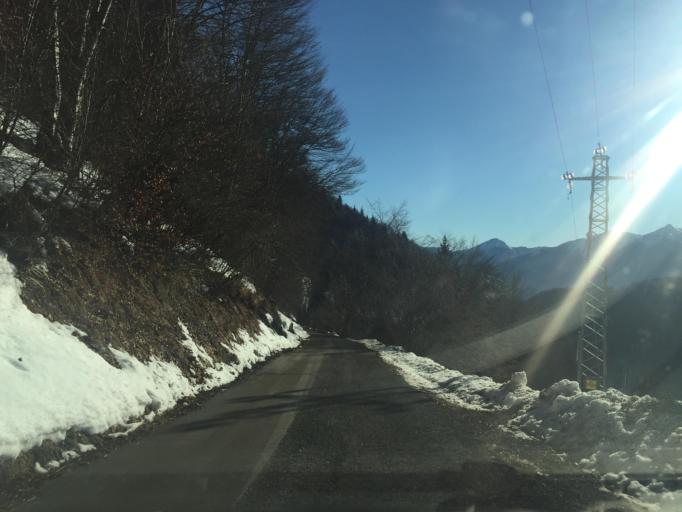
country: IT
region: Friuli Venezia Giulia
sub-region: Provincia di Udine
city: Lauco
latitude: 46.4542
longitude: 12.9283
